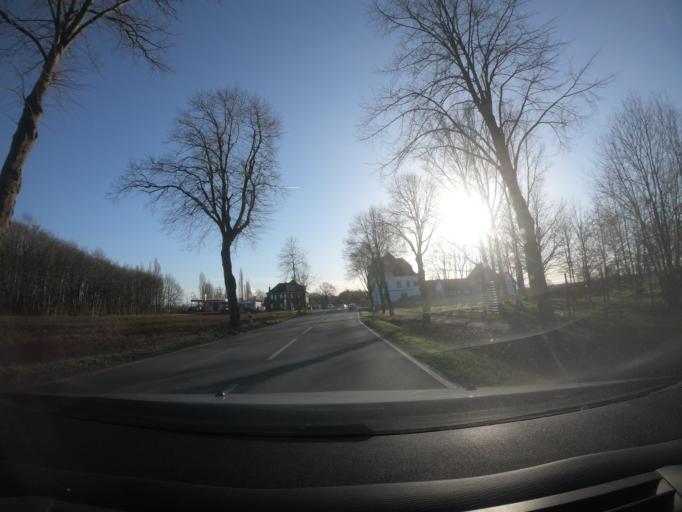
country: DE
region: North Rhine-Westphalia
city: Waltrop
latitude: 51.6416
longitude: 7.4341
